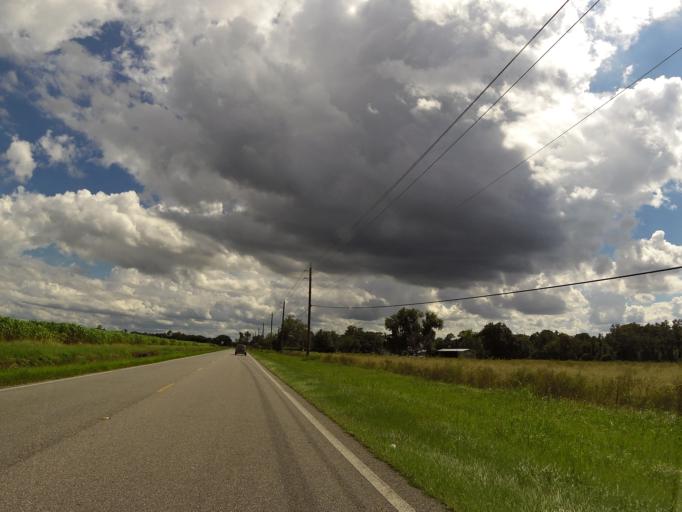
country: US
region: Florida
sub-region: Saint Johns County
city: Saint Augustine South
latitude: 29.8055
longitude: -81.4845
